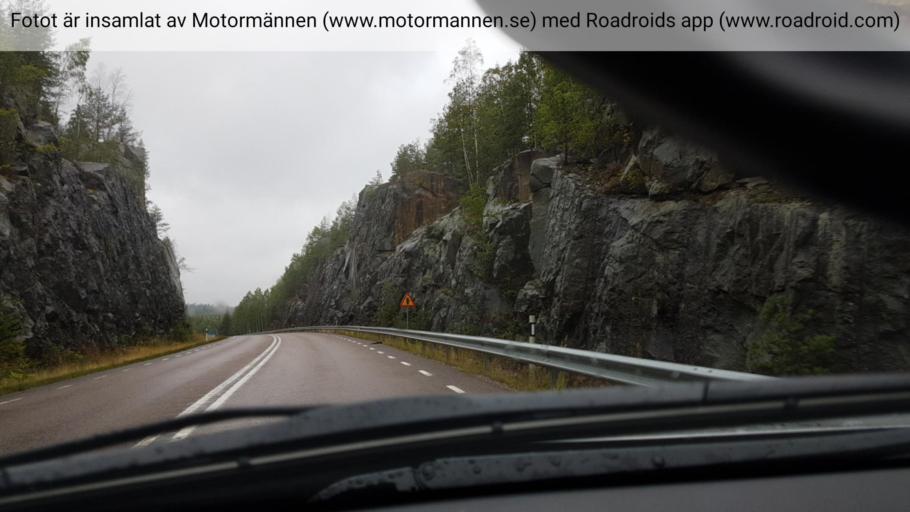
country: SE
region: Vaestra Goetaland
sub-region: Amals Kommun
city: Amal
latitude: 59.0803
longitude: 12.6217
